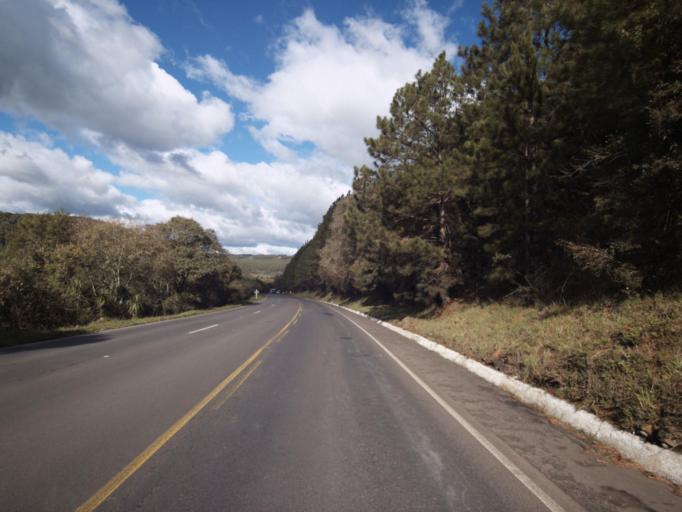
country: BR
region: Santa Catarina
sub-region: Joacaba
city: Joacaba
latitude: -27.0480
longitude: -51.7040
